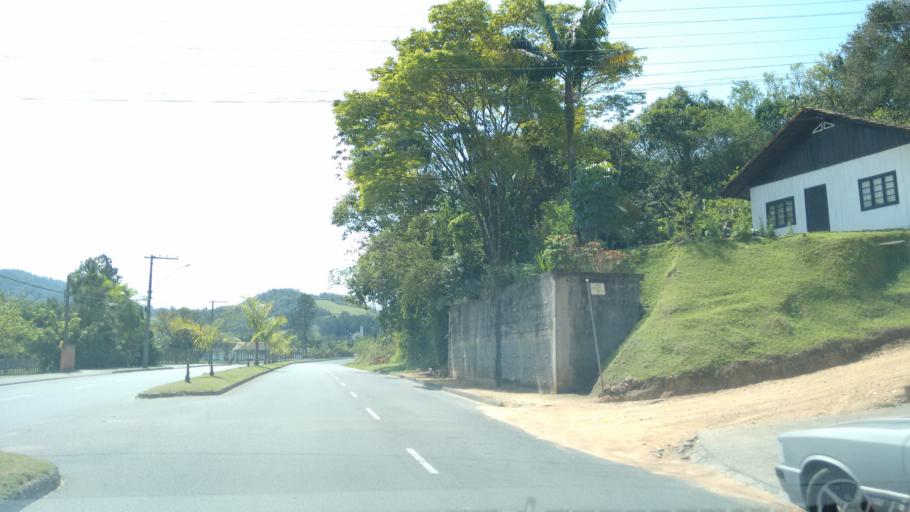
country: BR
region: Santa Catarina
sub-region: Pomerode
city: Pomerode
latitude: -26.7254
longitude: -49.1795
